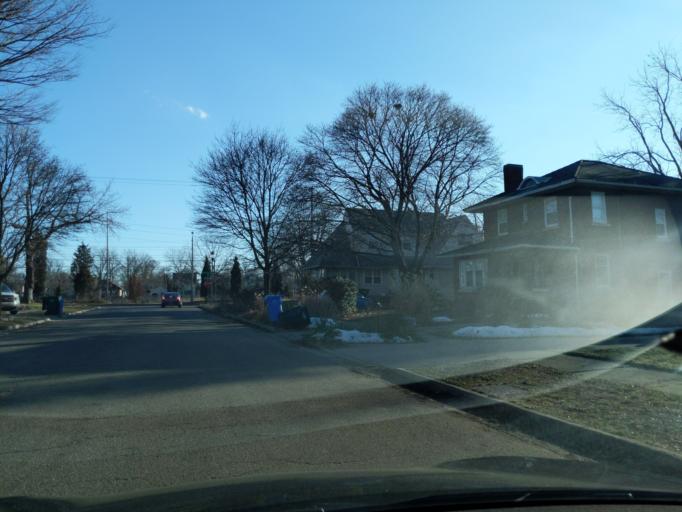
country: US
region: Michigan
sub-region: Ingham County
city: Lansing
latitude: 42.7272
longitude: -84.5728
